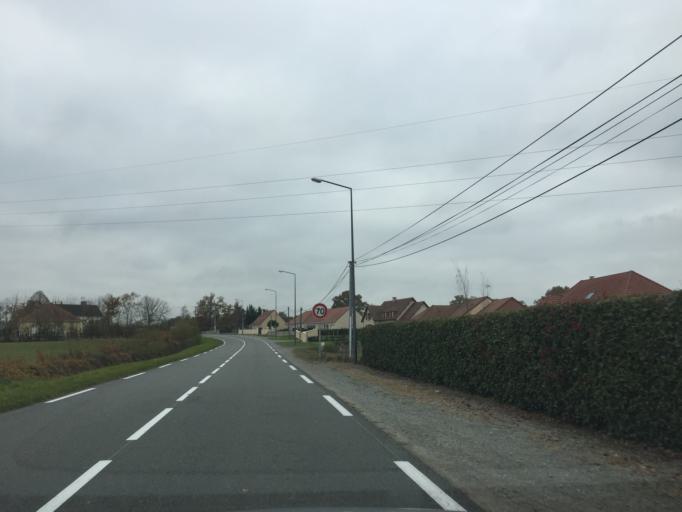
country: FR
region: Limousin
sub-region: Departement de la Creuse
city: Gouzon
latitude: 46.1849
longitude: 2.2324
